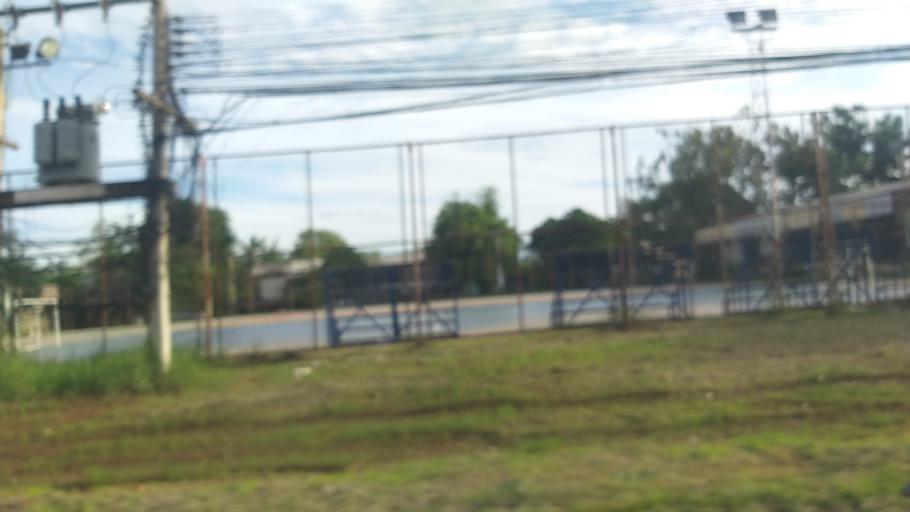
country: TH
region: Chaiyaphum
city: Ban Thaen
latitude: 16.4076
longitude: 102.3476
